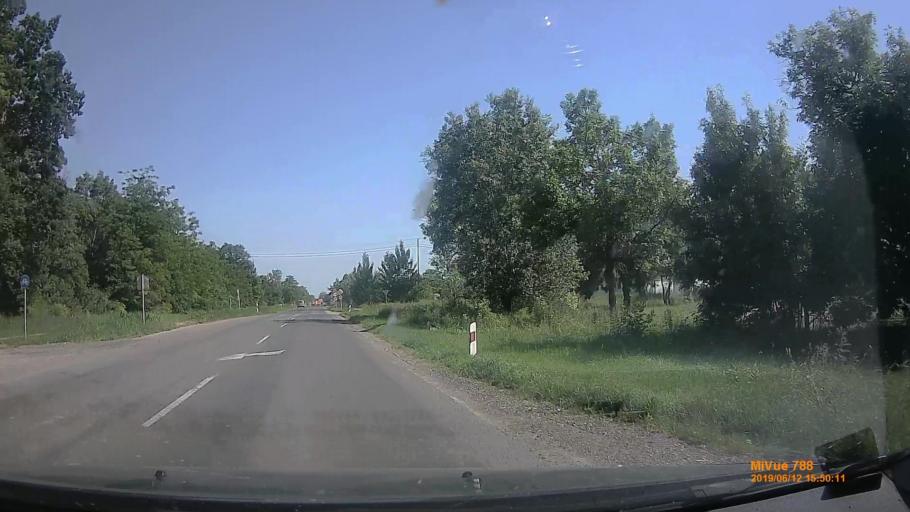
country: HU
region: Csongrad
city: Apatfalva
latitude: 46.1886
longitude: 20.5640
